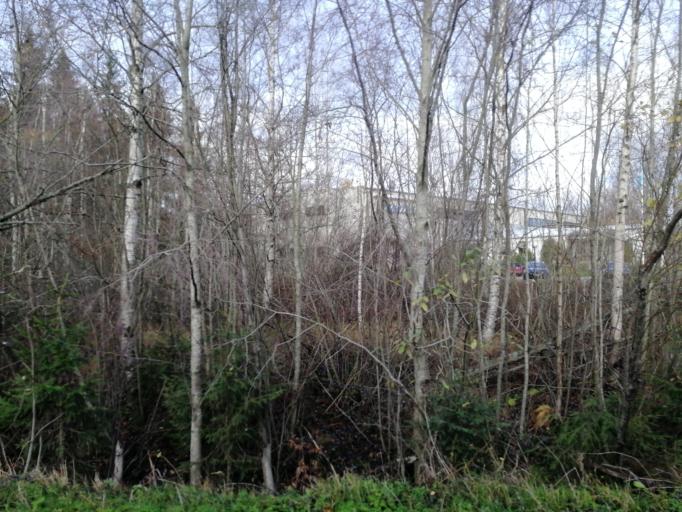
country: FI
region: Pirkanmaa
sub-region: Tampere
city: Tampere
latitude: 61.4533
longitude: 23.8825
